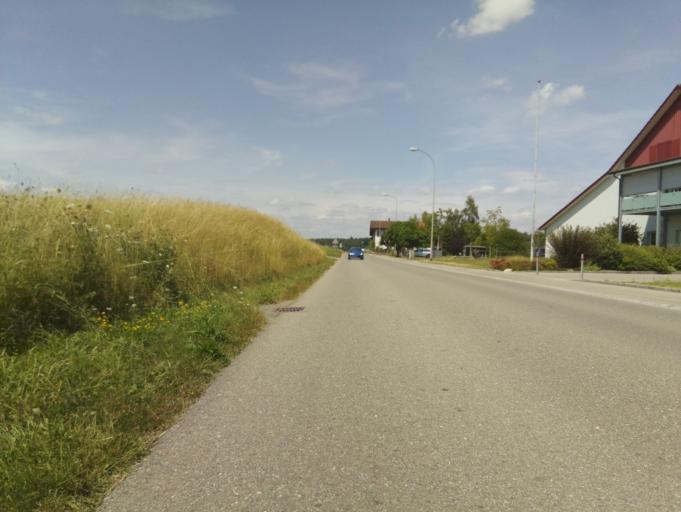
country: CH
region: Zurich
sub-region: Bezirk Andelfingen
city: Marthalen
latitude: 47.6308
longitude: 8.6491
